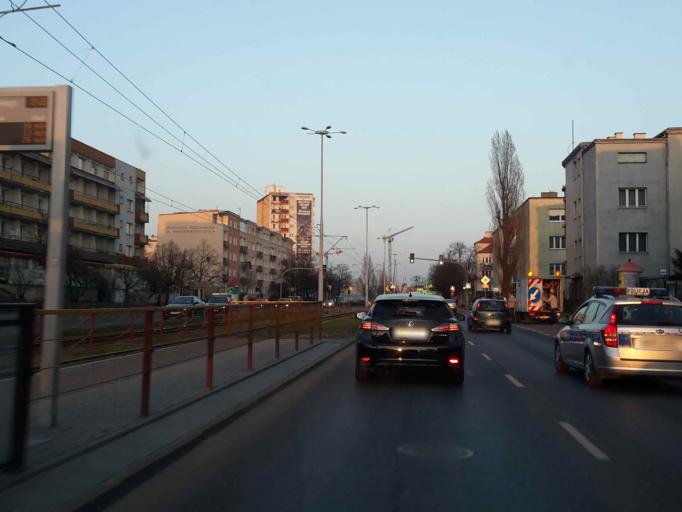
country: PL
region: Kujawsko-Pomorskie
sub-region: Torun
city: Torun
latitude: 53.0141
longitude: 18.5919
